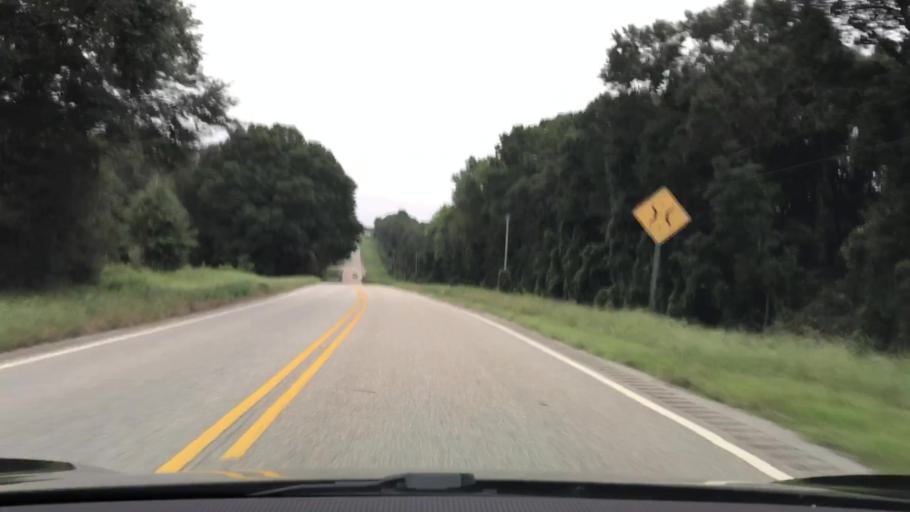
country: US
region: Alabama
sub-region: Covington County
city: Opp
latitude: 31.2938
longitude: -86.1437
